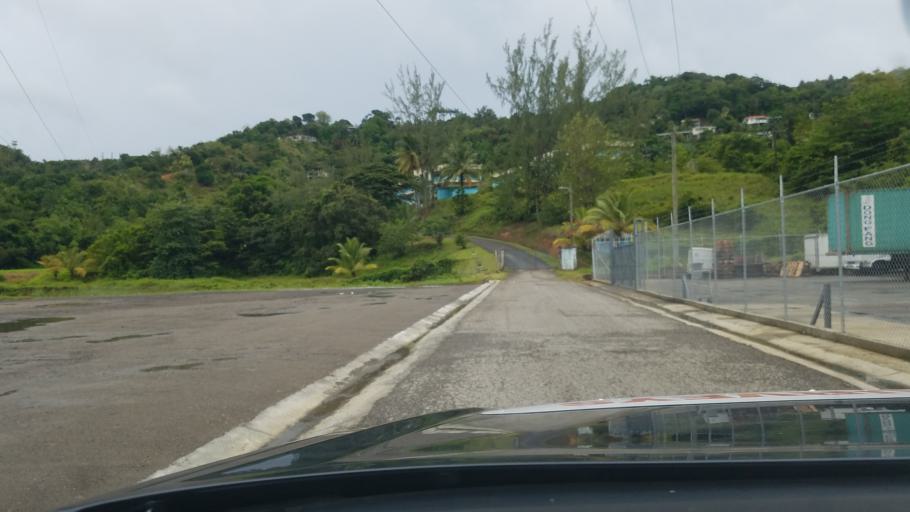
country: LC
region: Castries Quarter
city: Castries
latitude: 13.9872
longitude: -60.9999
